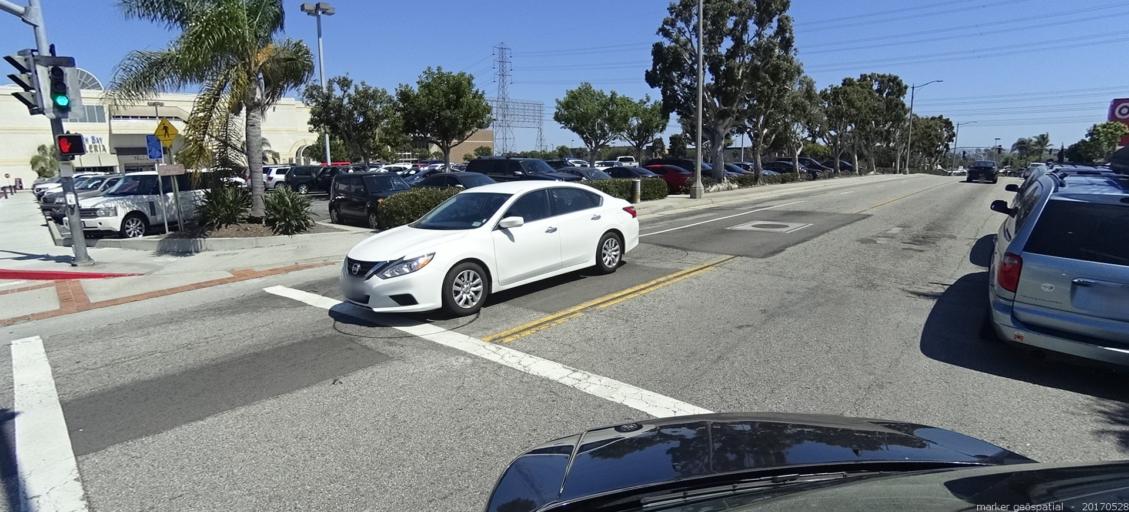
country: US
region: California
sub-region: Los Angeles County
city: Lawndale
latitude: 33.8710
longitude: -118.3569
